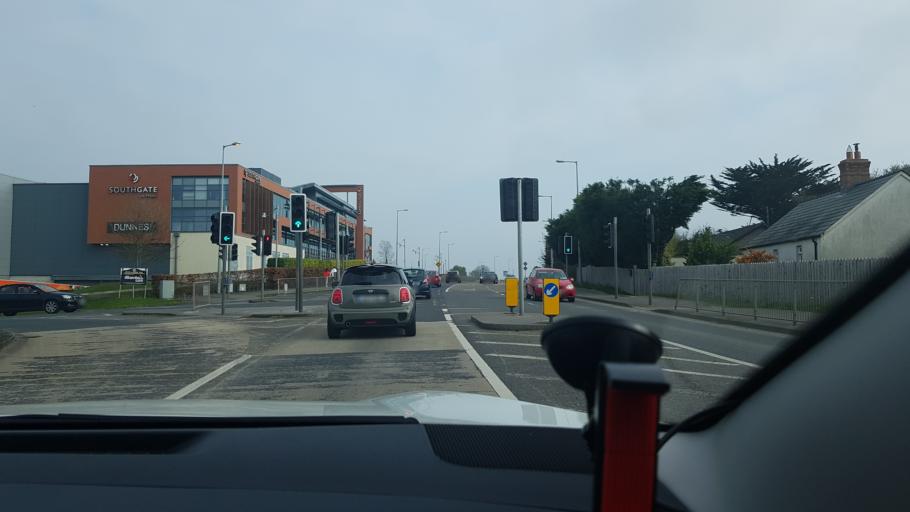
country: IE
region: Leinster
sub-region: Lu
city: Drogheda
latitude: 53.7024
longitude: -6.3129
